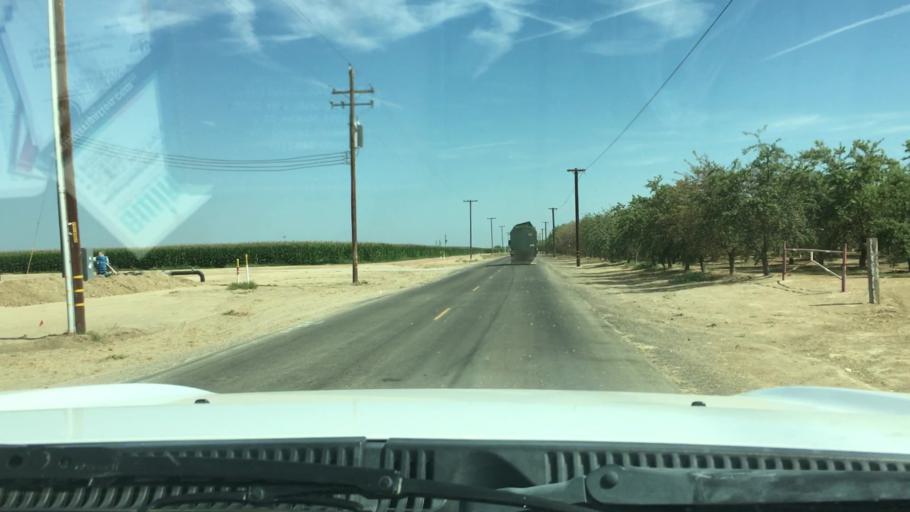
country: US
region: California
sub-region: Kern County
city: Shafter
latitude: 35.4746
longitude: -119.3680
